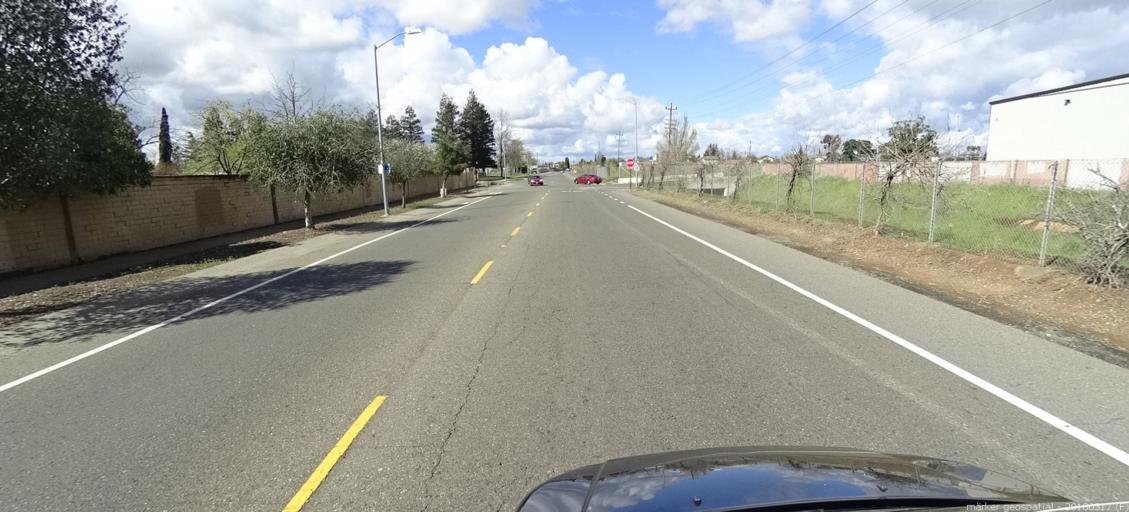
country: US
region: California
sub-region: Sacramento County
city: Florin
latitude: 38.4742
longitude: -121.3959
